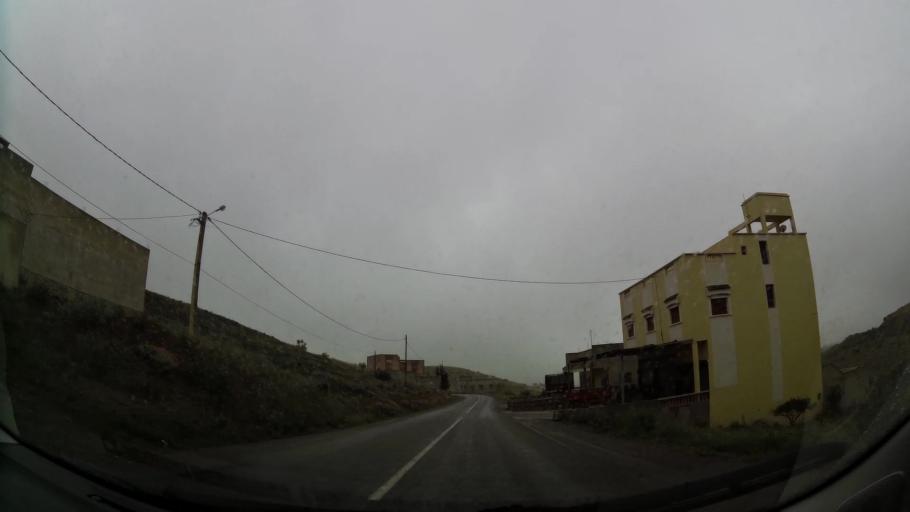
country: MA
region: Oriental
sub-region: Nador
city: Boudinar
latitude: 35.1283
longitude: -3.5822
